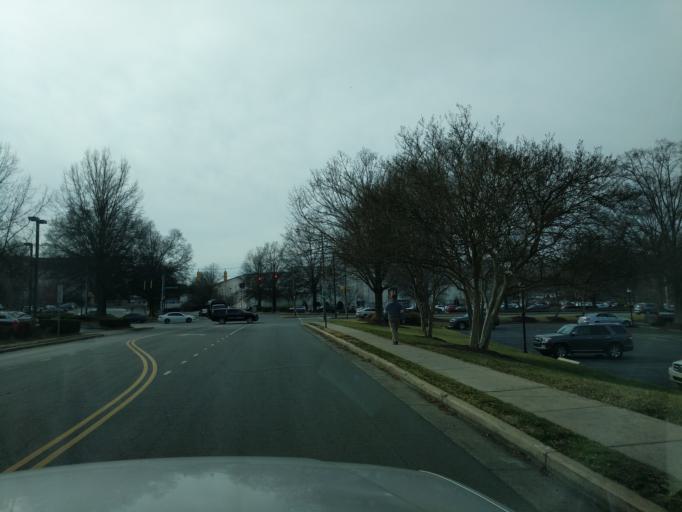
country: US
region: North Carolina
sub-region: Mecklenburg County
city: Charlotte
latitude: 35.1560
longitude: -80.8301
